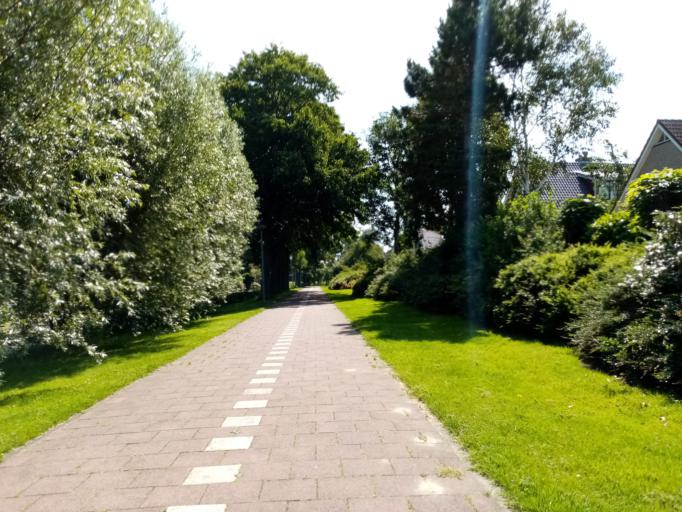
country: NL
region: South Holland
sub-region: Gemeente Katwijk
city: Katwijk aan den Rijn
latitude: 52.2078
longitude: 4.4305
